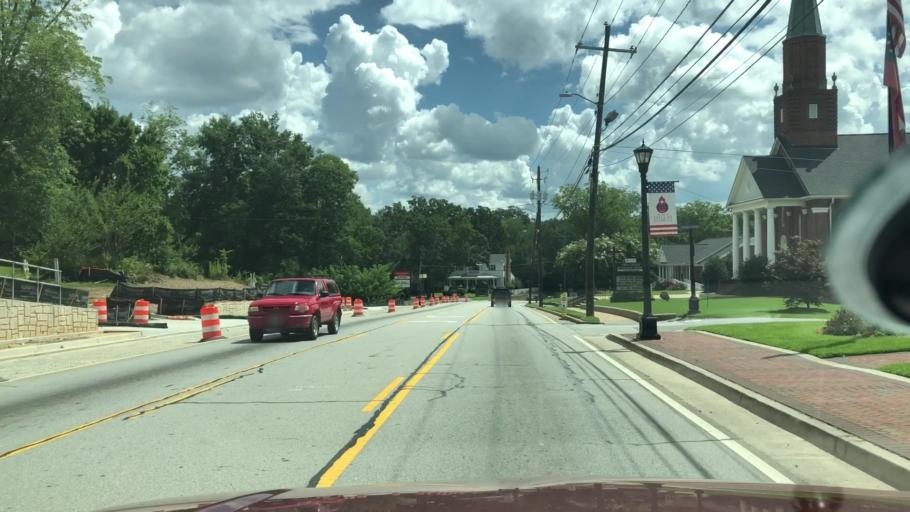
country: US
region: Georgia
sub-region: Paulding County
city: Dallas
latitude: 33.9246
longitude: -84.8407
